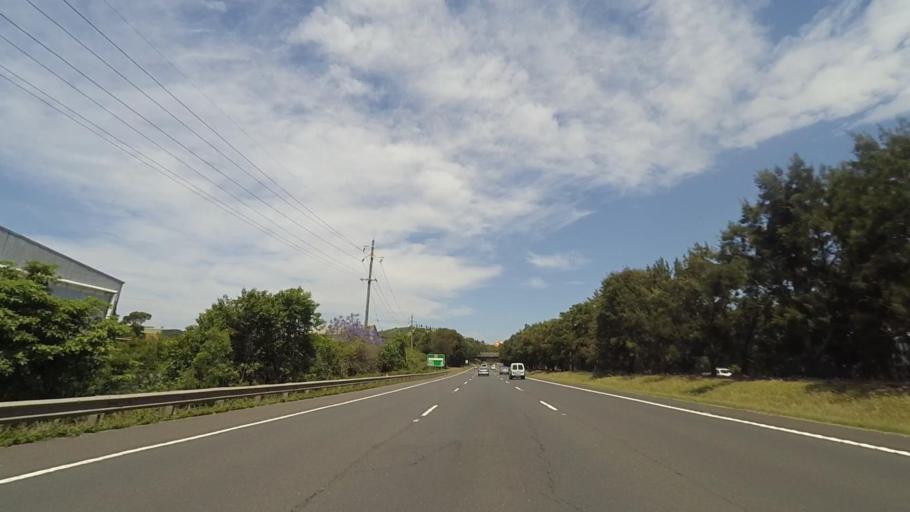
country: AU
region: New South Wales
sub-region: Wollongong
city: Berkeley
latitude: -34.4596
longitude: 150.8543
